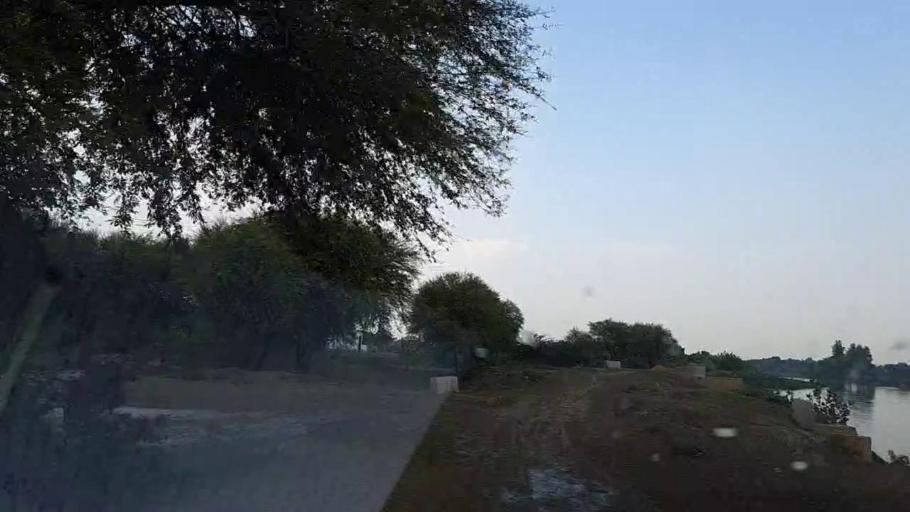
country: PK
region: Sindh
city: Daro Mehar
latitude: 24.7379
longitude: 68.1550
